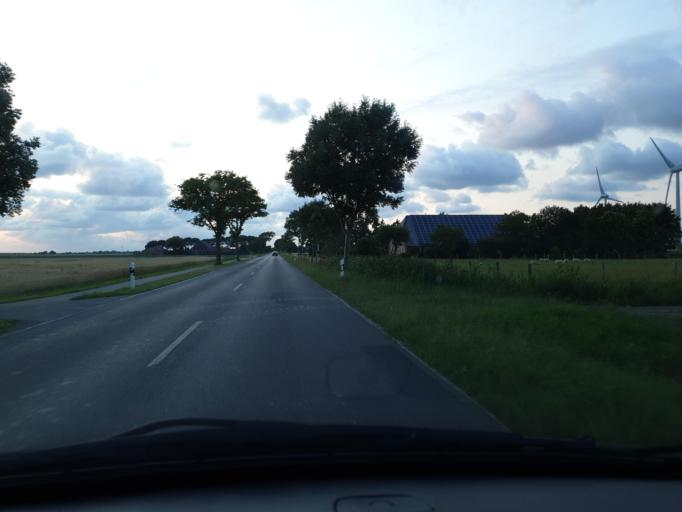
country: DE
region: Schleswig-Holstein
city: Friedrichskoog
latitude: 53.9764
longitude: 8.9211
